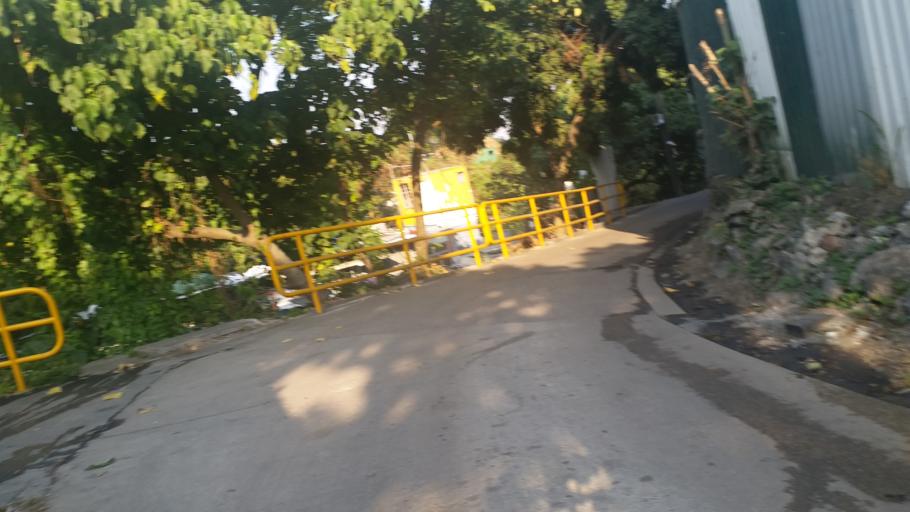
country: HK
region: Tuen Mun
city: Tuen Mun
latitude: 22.4179
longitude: 113.9724
